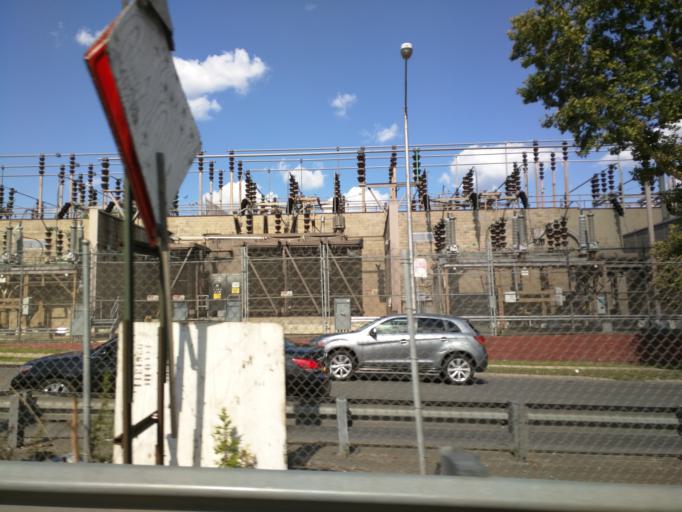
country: US
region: New York
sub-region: Queens County
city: Jamaica
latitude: 40.6989
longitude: -73.8145
